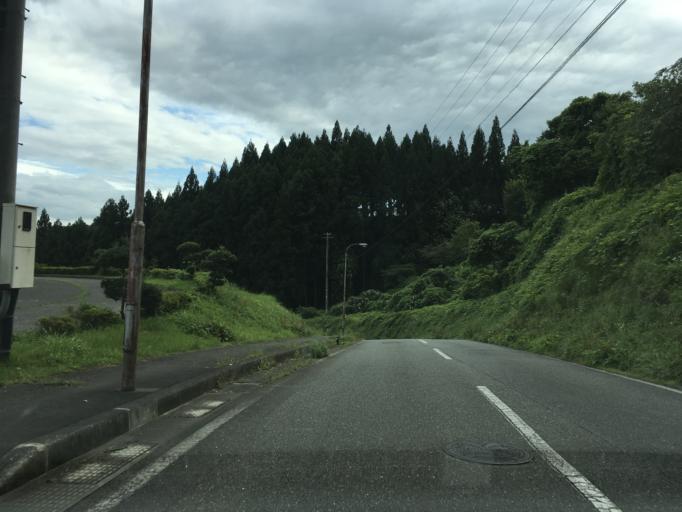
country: JP
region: Iwate
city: Ichinoseki
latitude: 38.9980
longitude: 141.2503
